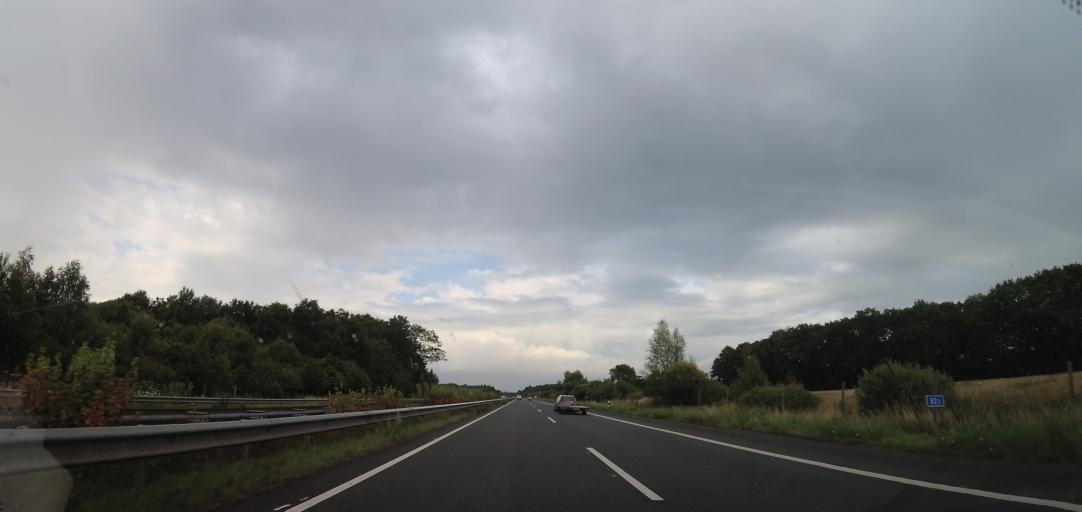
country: DE
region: North Rhine-Westphalia
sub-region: Regierungsbezirk Munster
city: Ochtrup
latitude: 52.2566
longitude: 7.1718
